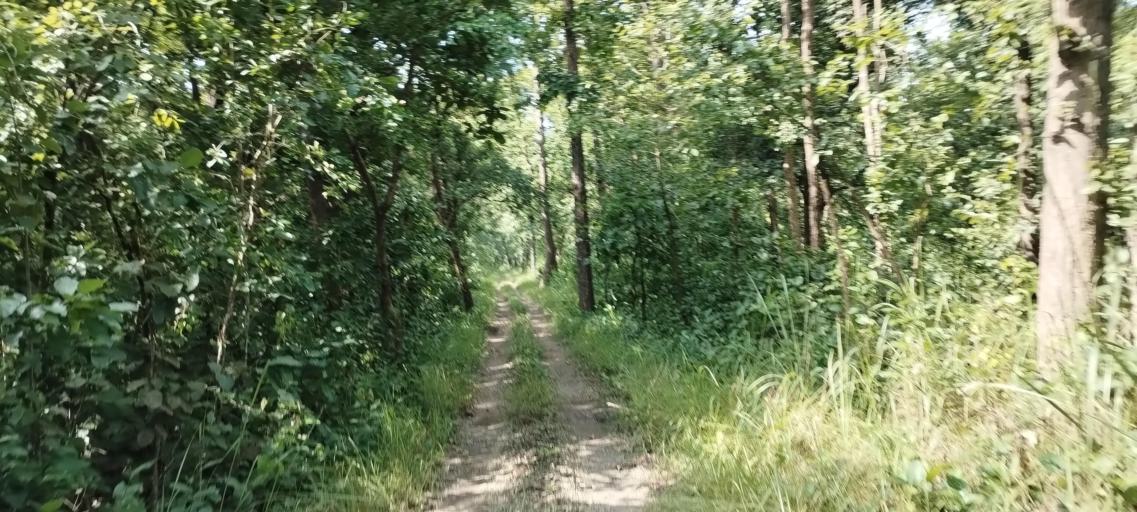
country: NP
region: Far Western
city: Tikapur
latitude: 28.5622
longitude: 81.2945
